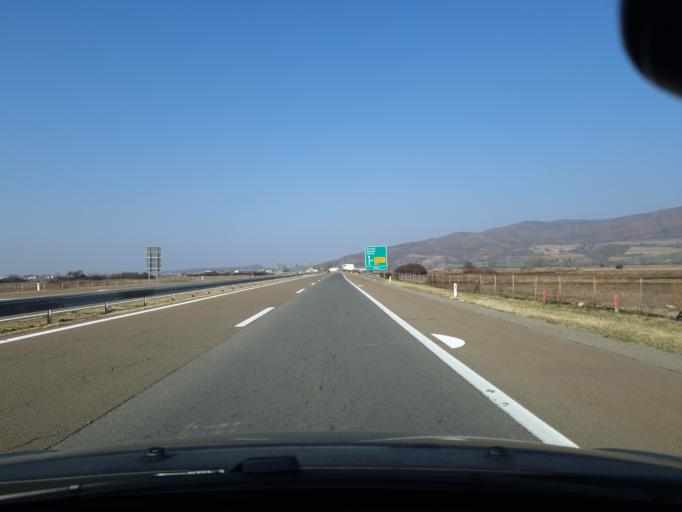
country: RS
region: Central Serbia
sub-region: Nisavski Okrug
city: Doljevac
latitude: 43.1847
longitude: 21.8608
